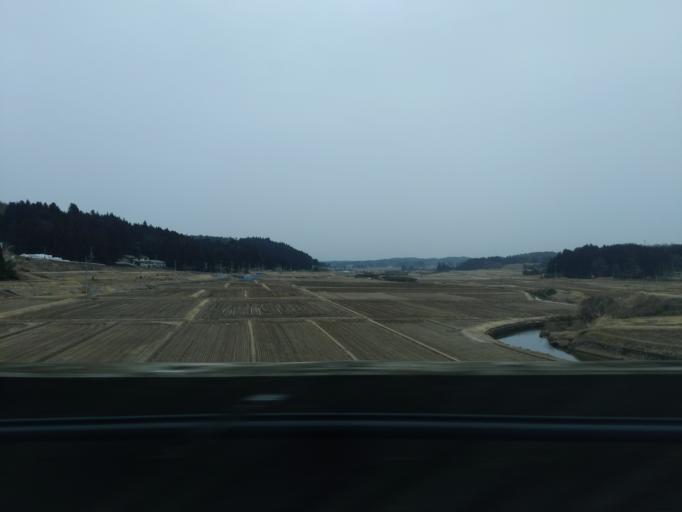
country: JP
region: Iwate
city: Ichinoseki
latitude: 38.8470
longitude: 141.1106
